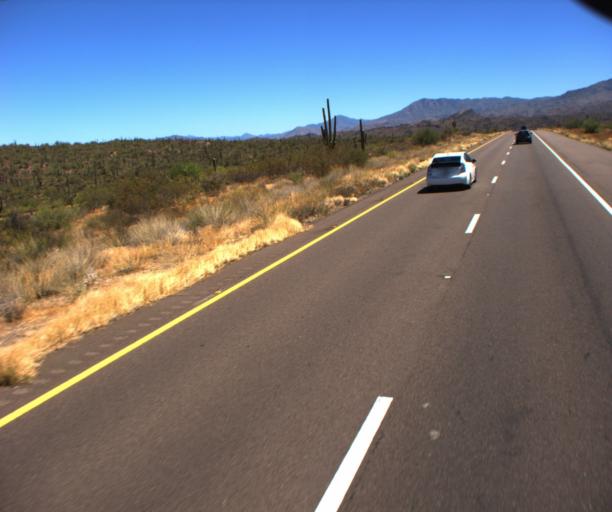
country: US
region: Arizona
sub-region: Maricopa County
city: Rio Verde
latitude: 33.6613
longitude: -111.5180
